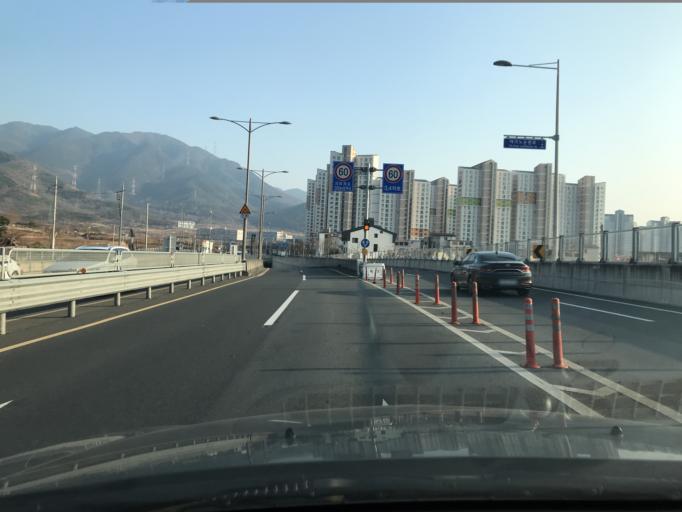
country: KR
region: Daegu
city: Hwawon
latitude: 35.7032
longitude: 128.4661
